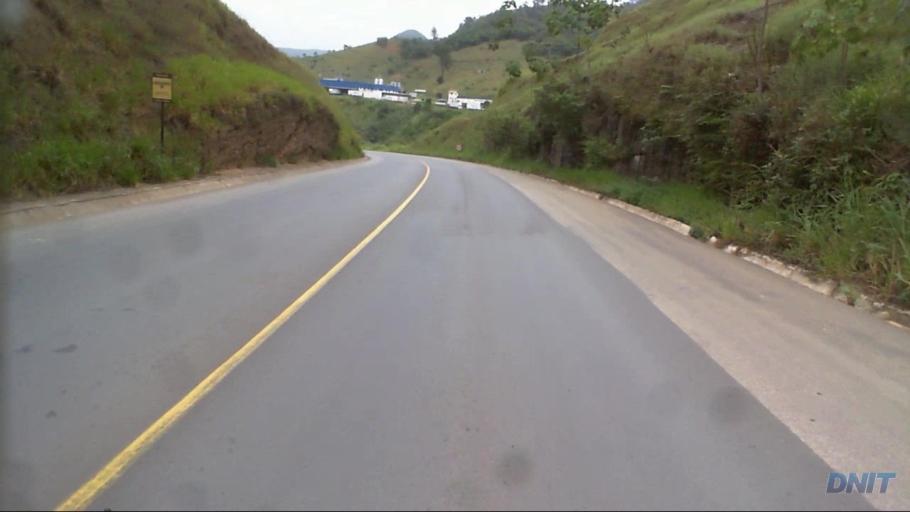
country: BR
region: Minas Gerais
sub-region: Coronel Fabriciano
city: Coronel Fabriciano
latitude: -19.5281
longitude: -42.6706
